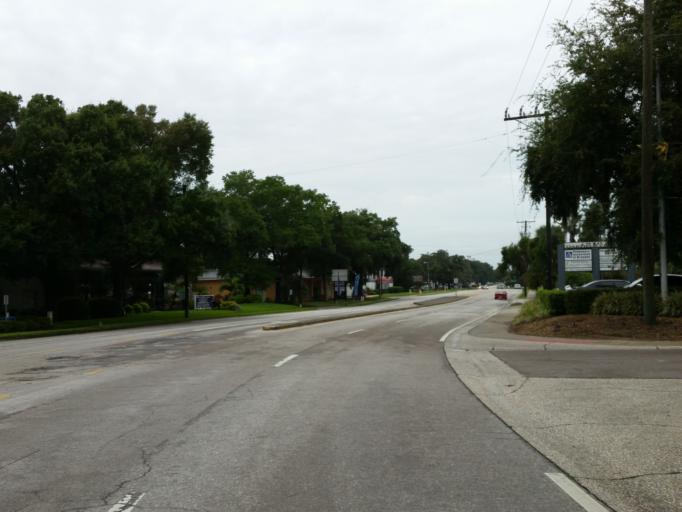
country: US
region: Florida
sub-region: Hillsborough County
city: Brandon
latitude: 27.9342
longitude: -82.2963
